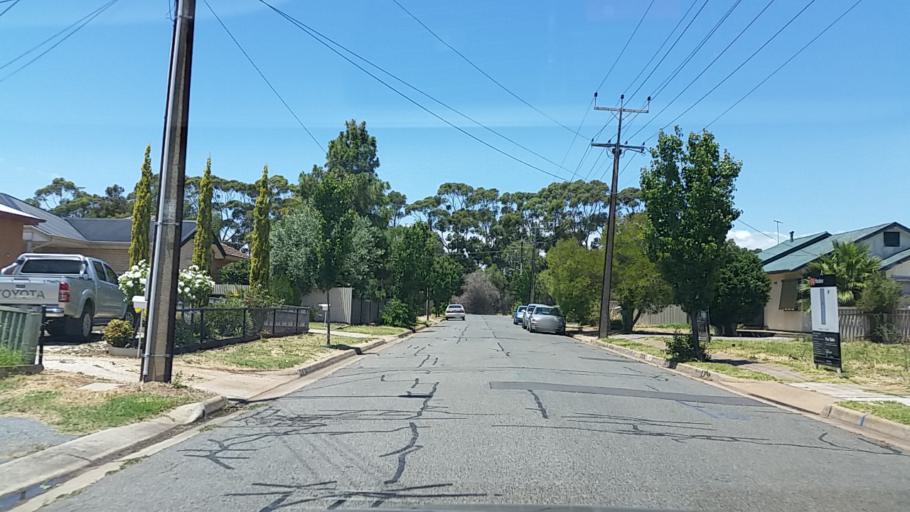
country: AU
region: South Australia
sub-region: Salisbury
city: Salisbury
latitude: -34.7673
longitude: 138.6405
